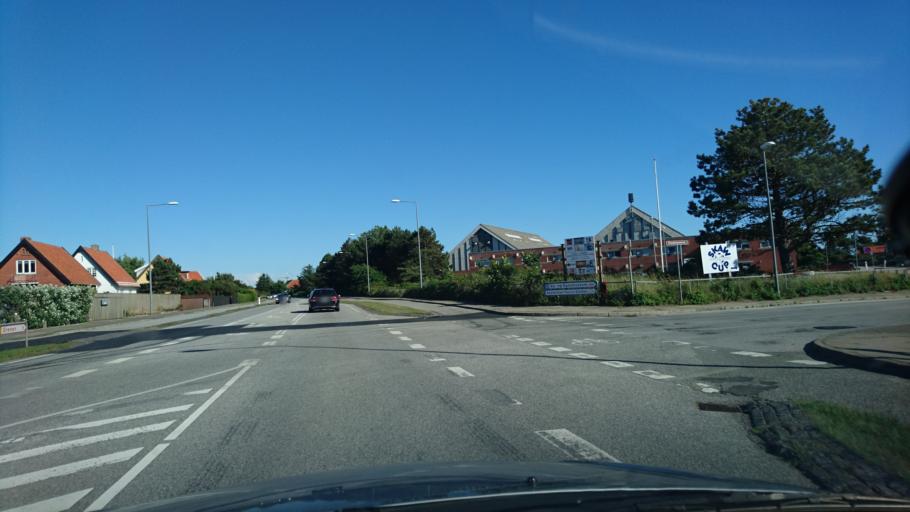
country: DK
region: North Denmark
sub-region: Frederikshavn Kommune
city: Skagen
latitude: 57.7234
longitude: 10.5655
